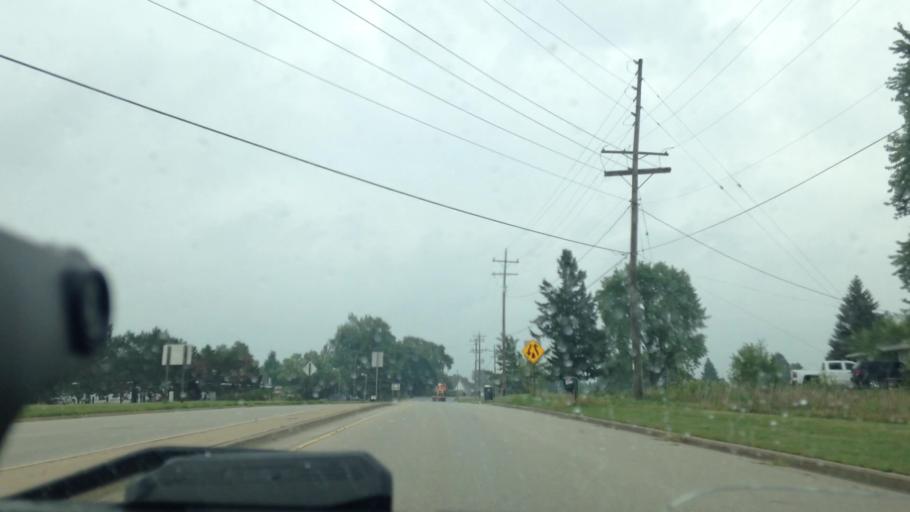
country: US
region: Wisconsin
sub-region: Washington County
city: Slinger
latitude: 43.3241
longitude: -88.2714
